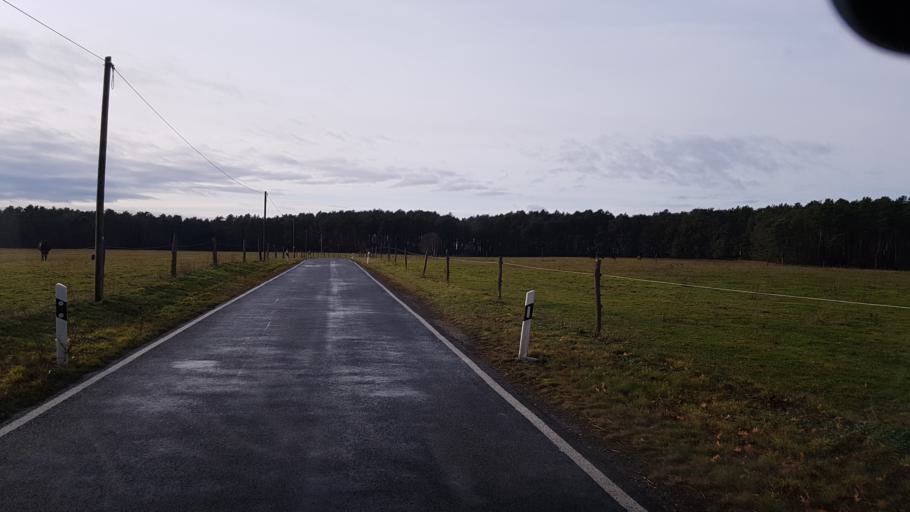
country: DE
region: Brandenburg
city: Bronkow
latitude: 51.6700
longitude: 13.9761
